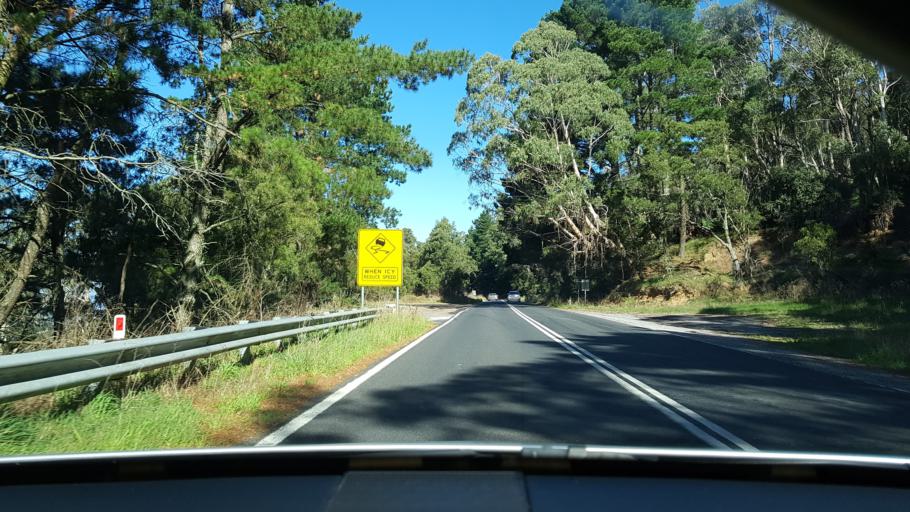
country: AU
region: New South Wales
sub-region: Lithgow
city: Bowenfels
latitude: -33.6489
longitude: 150.0499
